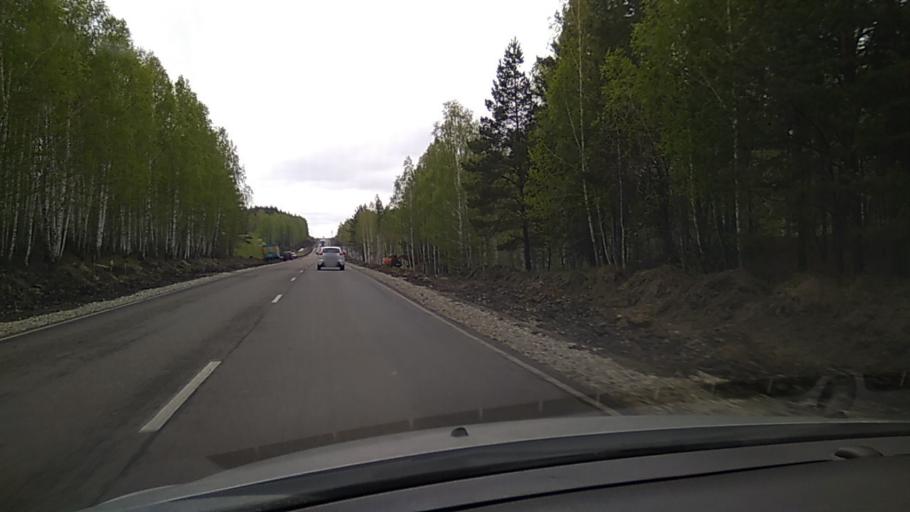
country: RU
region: Kurgan
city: Shadrinsk
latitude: 56.1428
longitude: 63.5080
